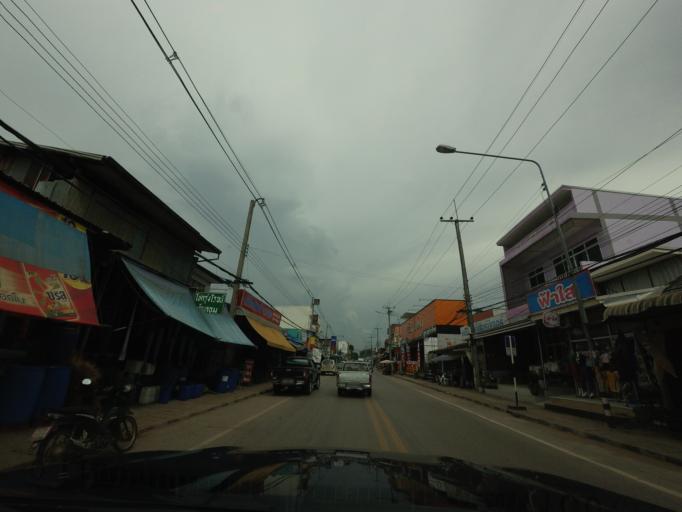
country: TH
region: Changwat Nong Bua Lamphu
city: Si Bun Rueang
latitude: 16.9661
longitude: 102.2729
